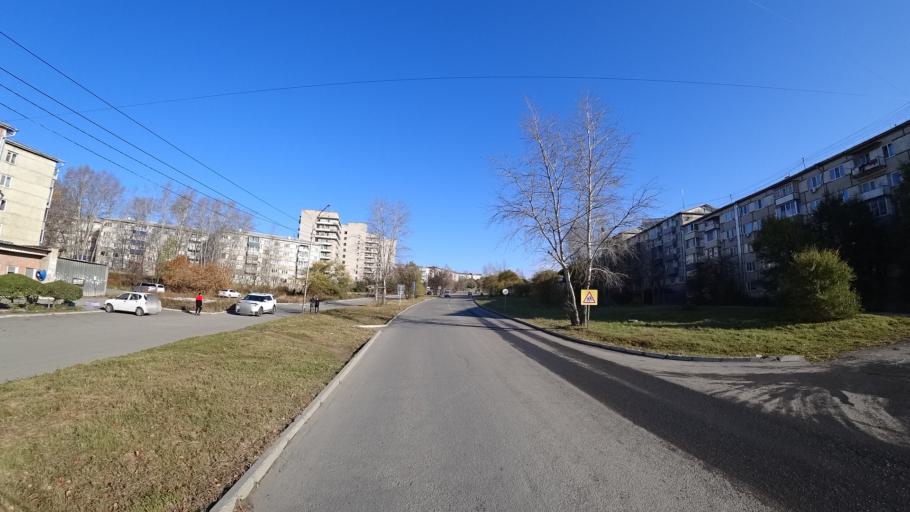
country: RU
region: Khabarovsk Krai
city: Amursk
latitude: 50.2379
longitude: 136.9111
